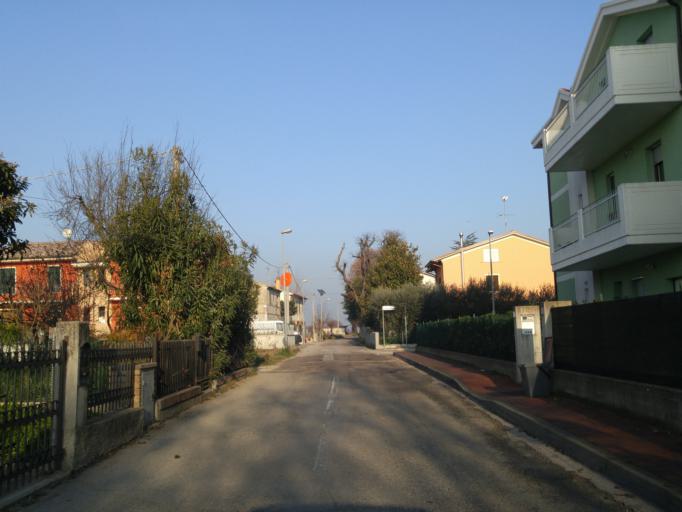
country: IT
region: The Marches
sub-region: Provincia di Pesaro e Urbino
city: Lucrezia
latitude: 43.7688
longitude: 12.9501
